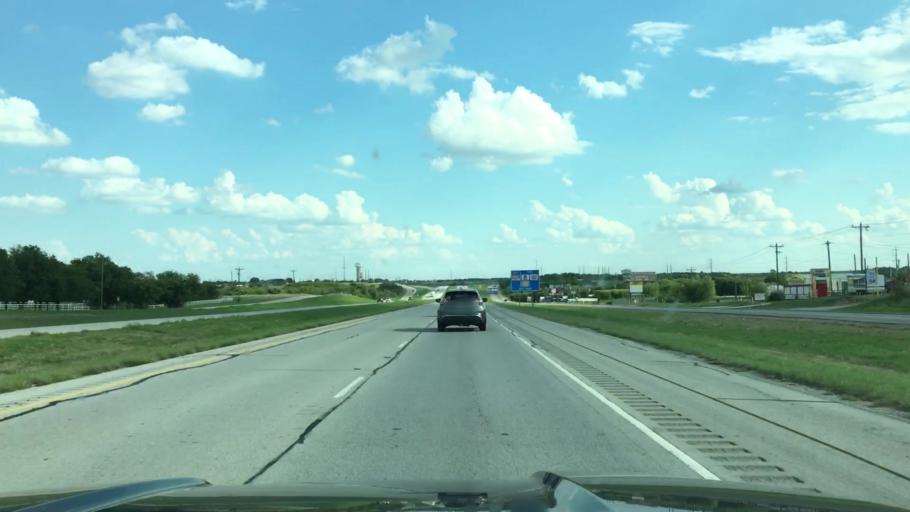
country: US
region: Texas
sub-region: Tarrant County
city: Pecan Acres
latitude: 32.9840
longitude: -97.4273
